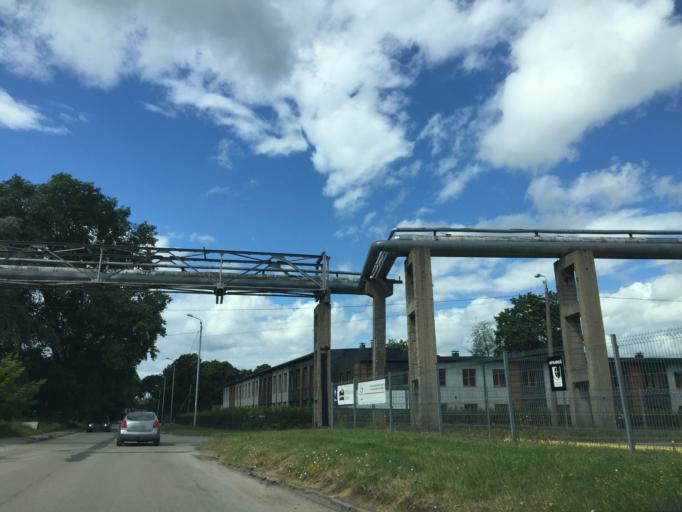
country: LV
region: Marupe
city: Marupe
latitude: 56.9441
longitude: 24.0390
